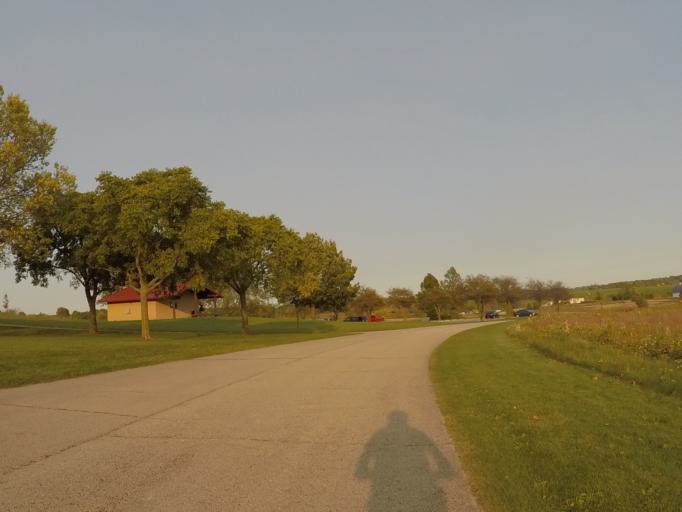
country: US
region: Wisconsin
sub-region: Dane County
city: Verona
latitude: 42.9975
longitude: -89.5203
